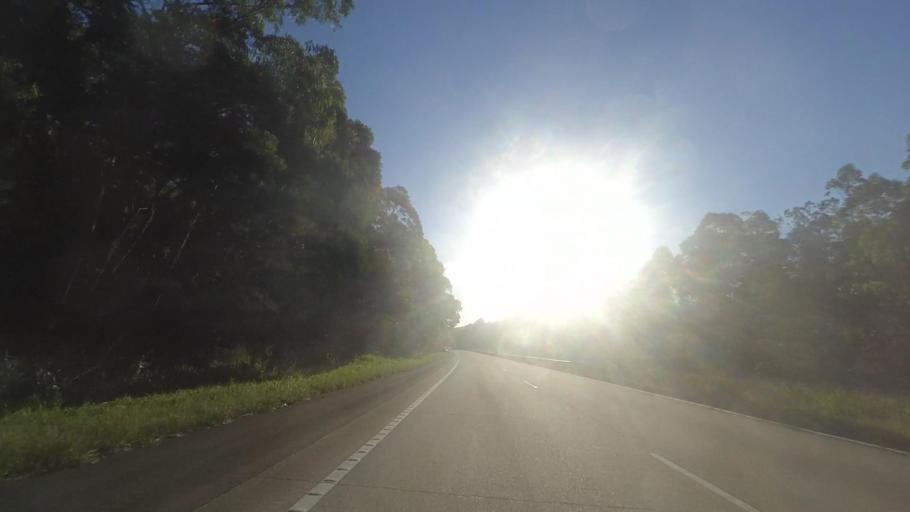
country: AU
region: New South Wales
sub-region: Great Lakes
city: Bulahdelah
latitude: -32.3757
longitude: 152.2770
